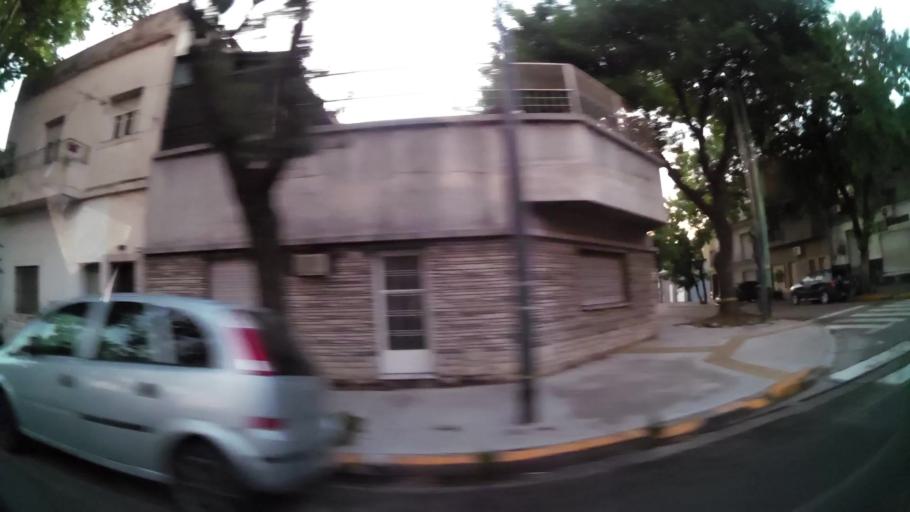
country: AR
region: Buenos Aires F.D.
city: Villa Lugano
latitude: -34.6413
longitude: -58.4351
